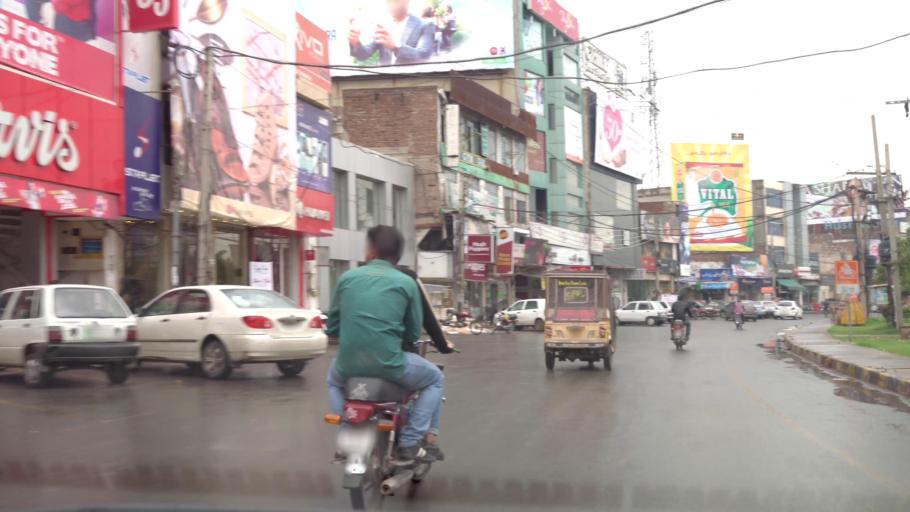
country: PK
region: Punjab
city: Faisalabad
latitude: 31.4121
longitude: 73.1146
